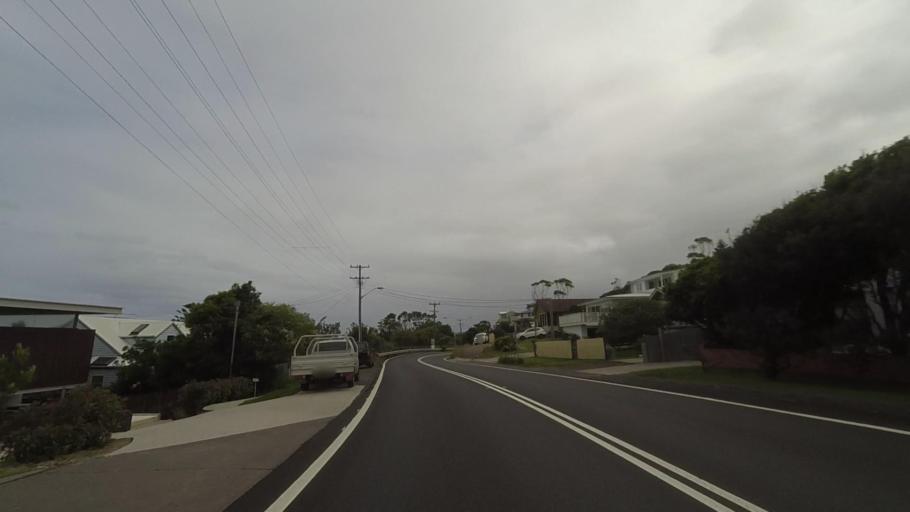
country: AU
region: New South Wales
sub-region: Wollongong
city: Bulli
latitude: -34.2814
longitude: 150.9529
